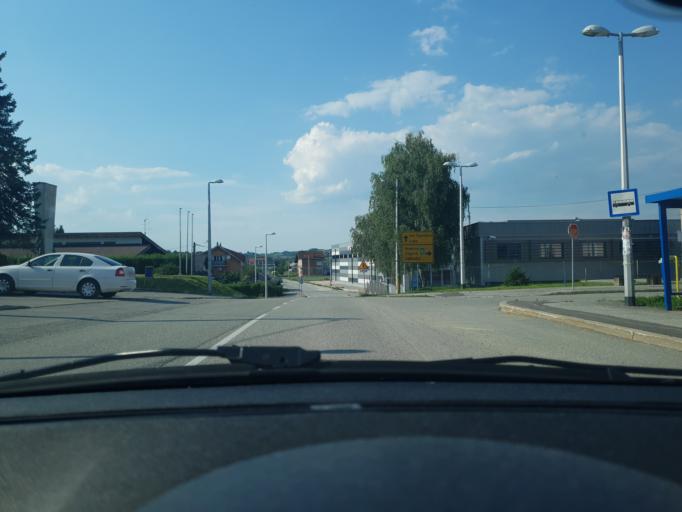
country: HR
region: Zagrebacka
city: Pojatno
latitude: 45.9321
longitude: 15.8149
